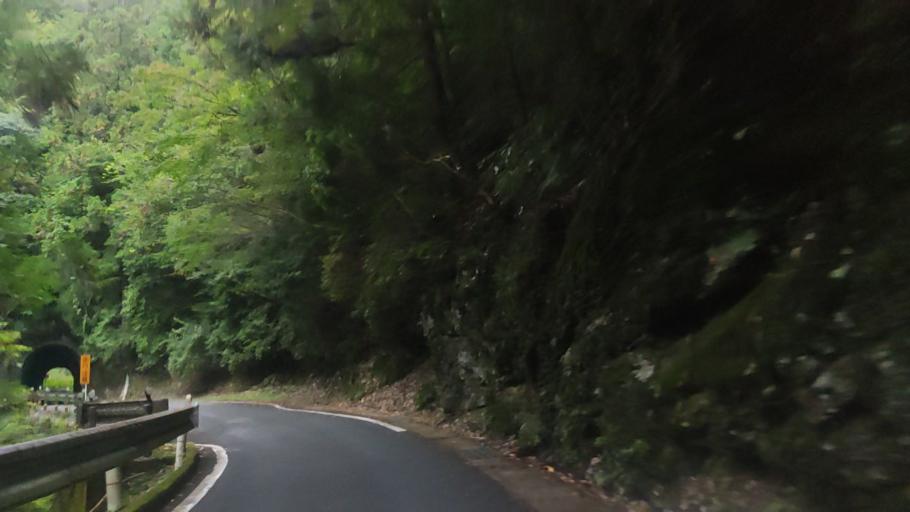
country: JP
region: Wakayama
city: Koya
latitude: 34.2426
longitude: 135.6524
